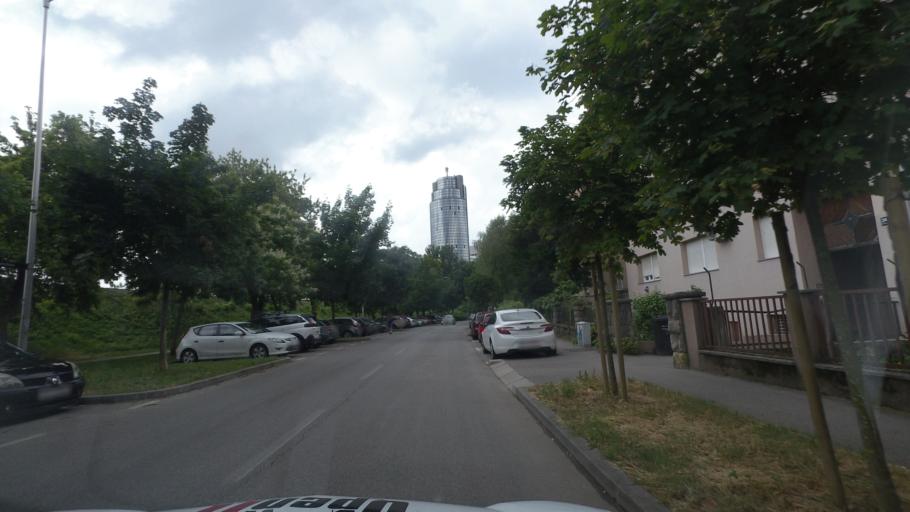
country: HR
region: Grad Zagreb
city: Zagreb - Centar
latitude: 45.8055
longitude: 15.9628
